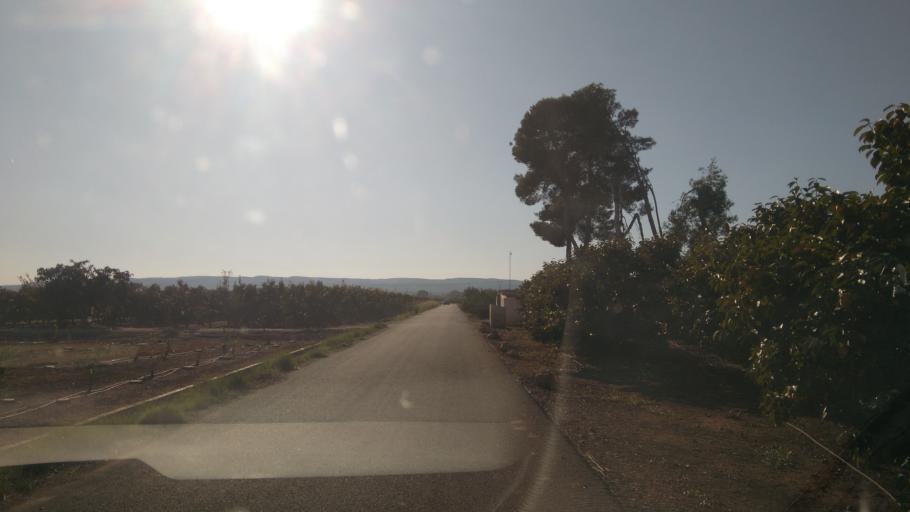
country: ES
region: Valencia
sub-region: Provincia de Valencia
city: Masalaves
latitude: 39.1784
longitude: -0.5366
